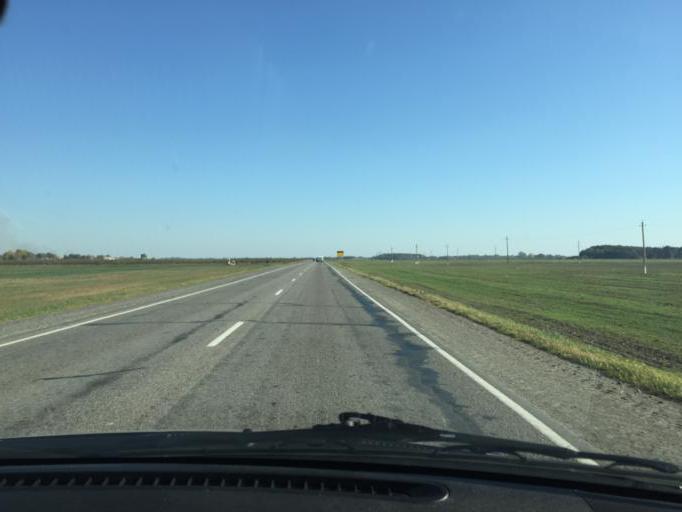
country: BY
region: Gomel
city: Turaw
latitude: 52.0611
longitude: 27.7951
